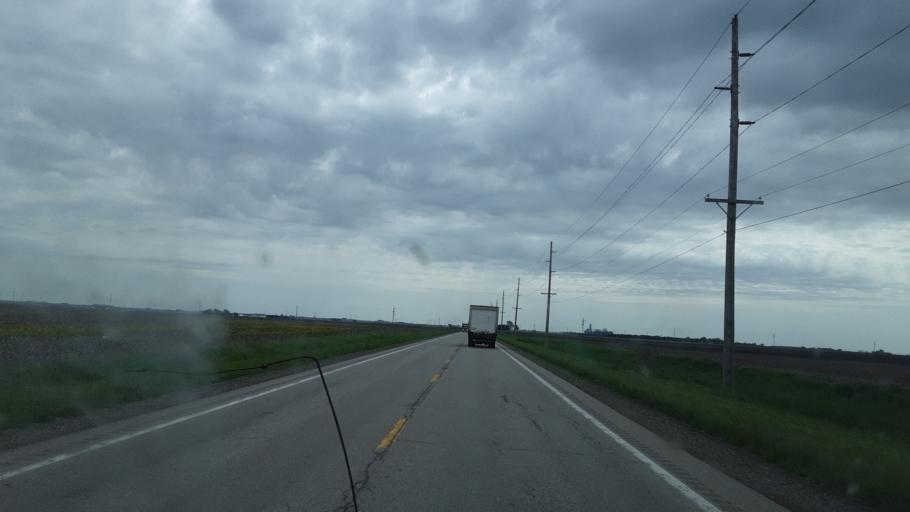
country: US
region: Illinois
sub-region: Tazewell County
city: Delavan
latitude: 40.3067
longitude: -89.5342
